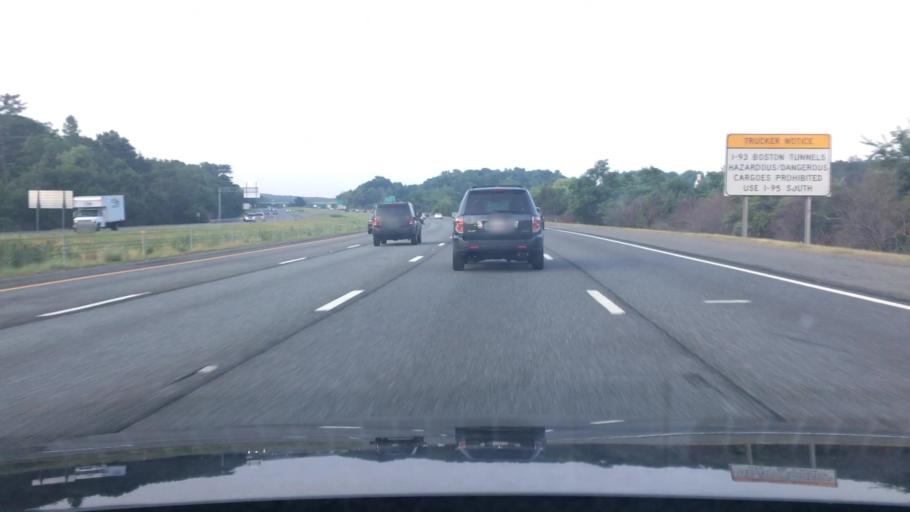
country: US
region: Massachusetts
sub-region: Essex County
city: Danvers
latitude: 42.5760
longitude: -70.9691
